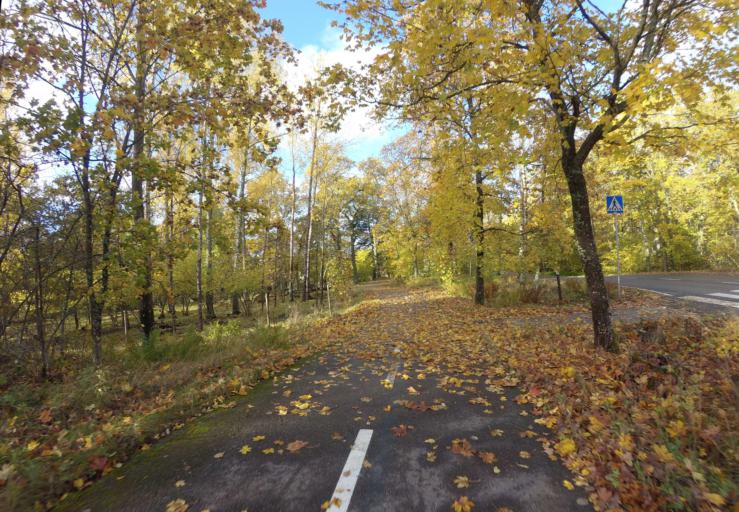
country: FI
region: Varsinais-Suomi
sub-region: Turku
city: Raisio
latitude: 60.4269
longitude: 22.1413
